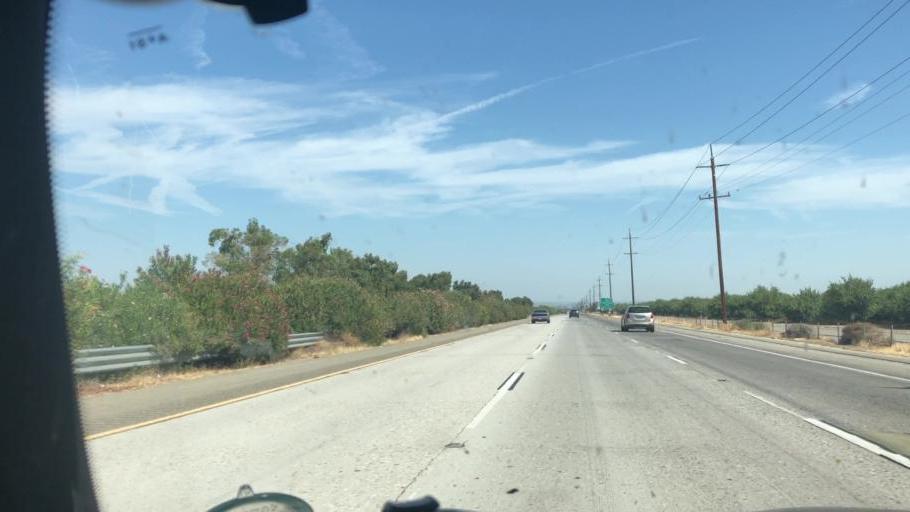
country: US
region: California
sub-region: Kern County
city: Weedpatch
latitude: 35.0416
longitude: -118.9626
